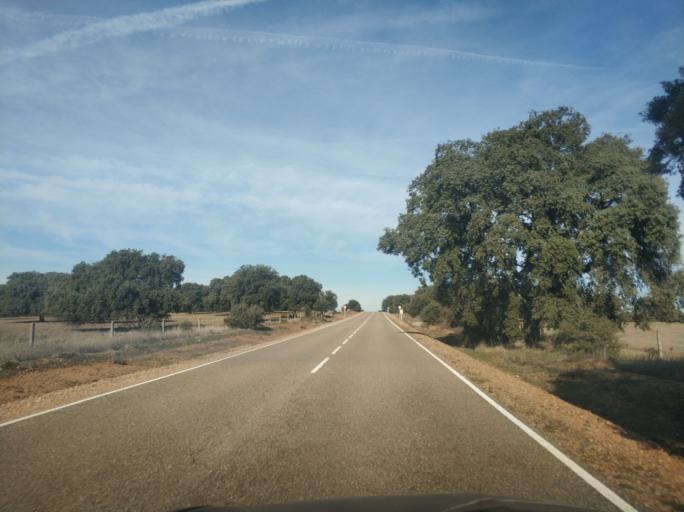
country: ES
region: Castille and Leon
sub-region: Provincia de Salamanca
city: Parada de Arriba
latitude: 40.9998
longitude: -5.8265
